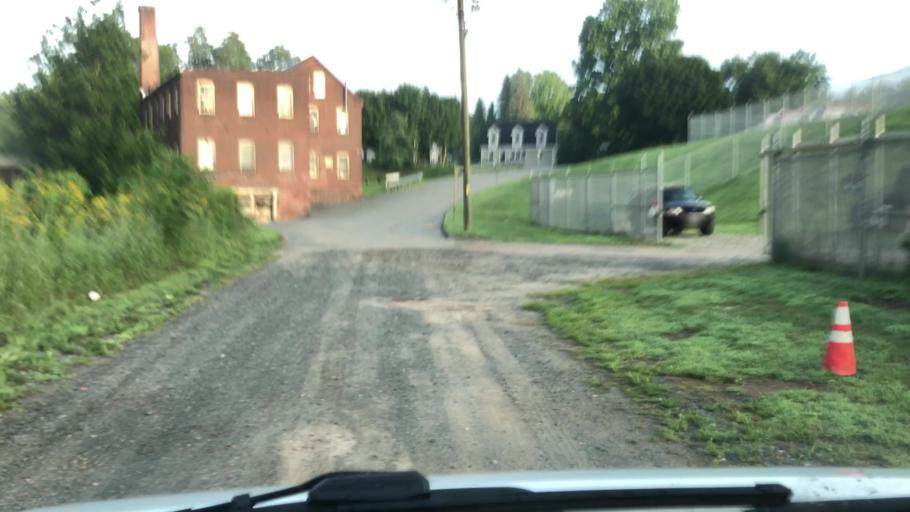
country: US
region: Massachusetts
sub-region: Franklin County
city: Greenfield
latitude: 42.5834
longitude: -72.6032
